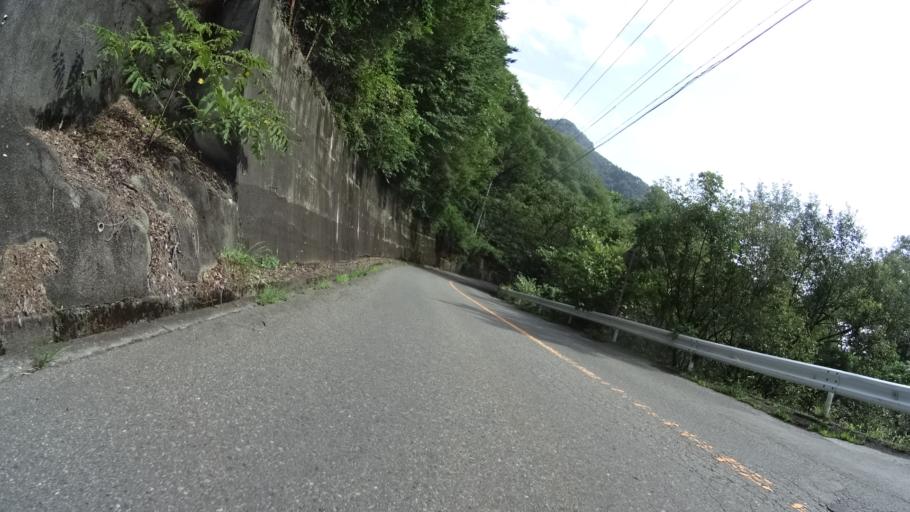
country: JP
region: Yamanashi
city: Kofu-shi
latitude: 35.7418
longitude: 138.5674
